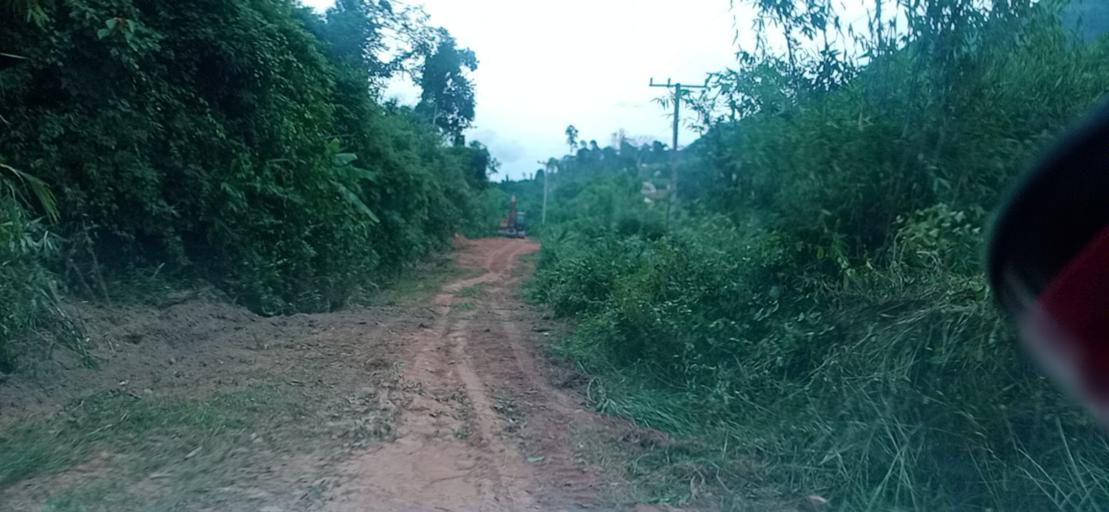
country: TH
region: Changwat Bueng Kan
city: Pak Khat
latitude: 18.5594
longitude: 103.2475
